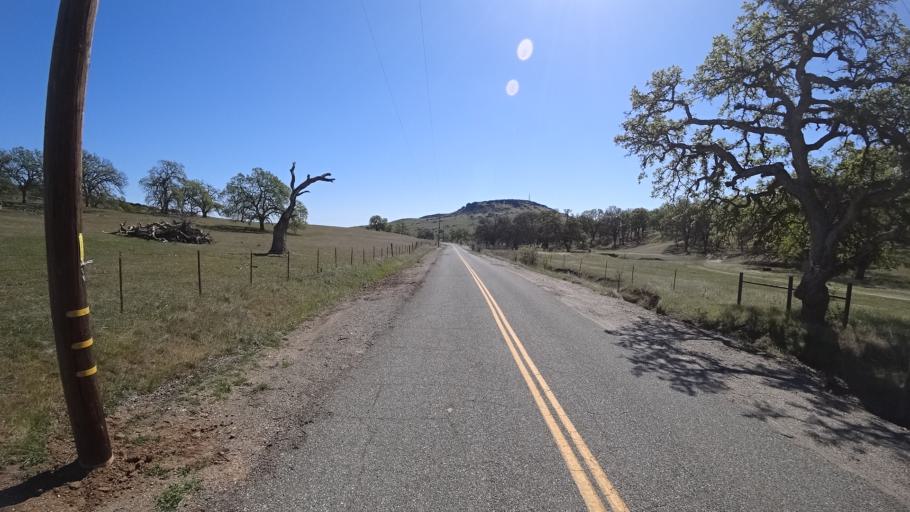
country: US
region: California
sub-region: Glenn County
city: Orland
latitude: 39.7648
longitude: -122.3449
